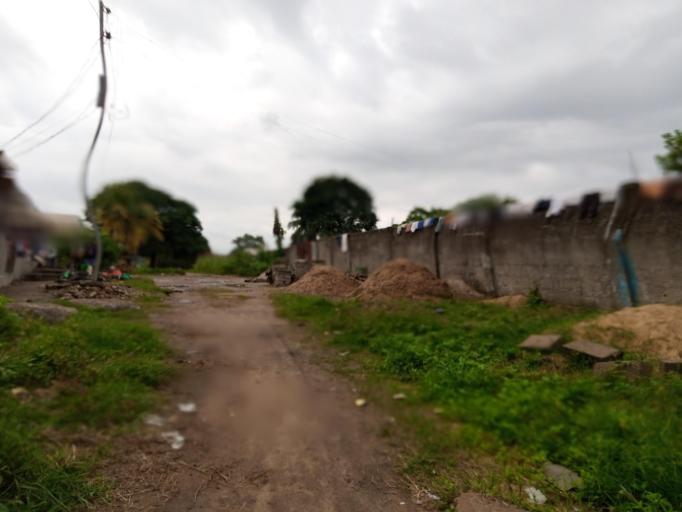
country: SL
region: Eastern Province
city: Kenema
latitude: 7.8610
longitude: -11.1962
